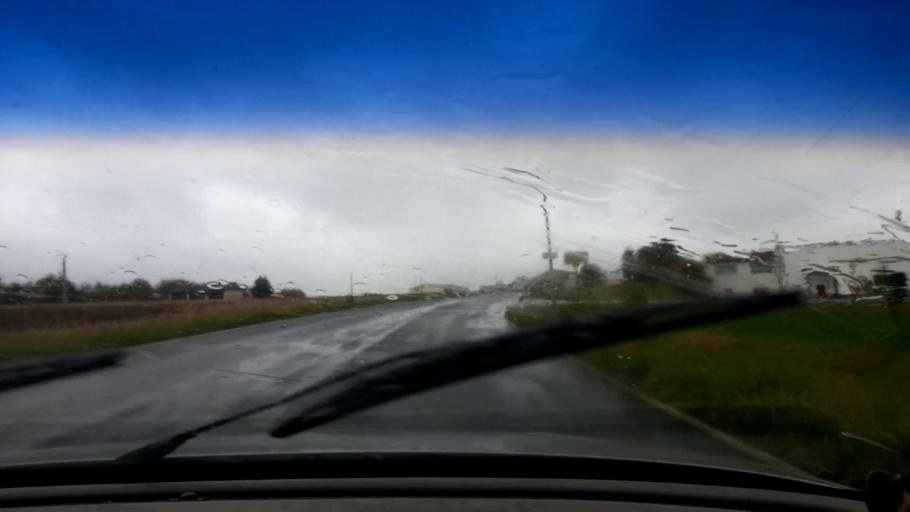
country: DE
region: Bavaria
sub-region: Upper Franconia
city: Stadelhofen
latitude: 50.0013
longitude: 11.2037
